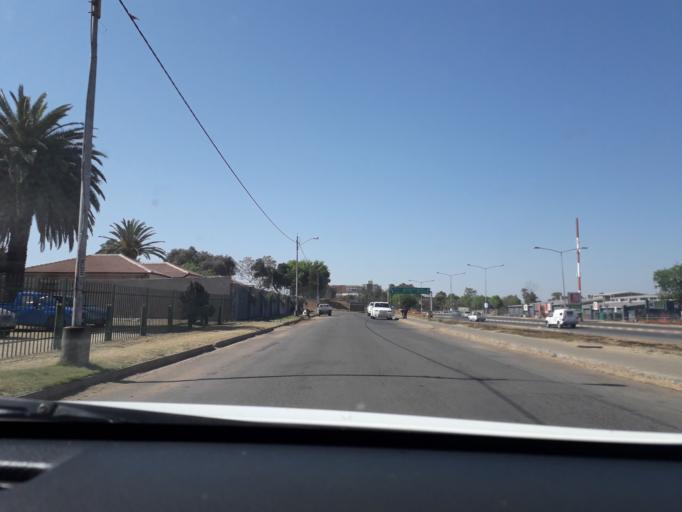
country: ZA
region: Gauteng
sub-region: City of Johannesburg Metropolitan Municipality
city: Modderfontein
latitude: -26.0973
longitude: 28.2230
